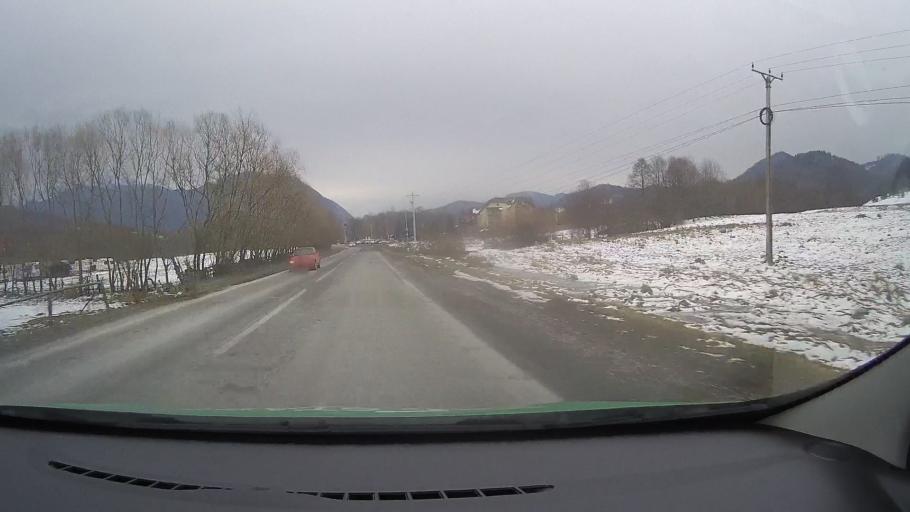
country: RO
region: Brasov
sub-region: Oras Rasnov
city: Rasnov
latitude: 45.5559
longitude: 25.4782
